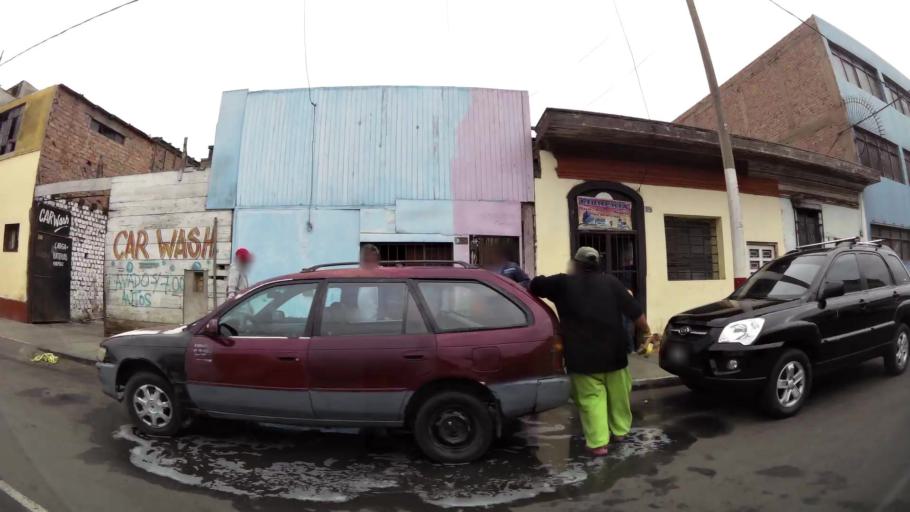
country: PE
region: Callao
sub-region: Callao
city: Callao
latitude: -12.0636
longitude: -77.1457
